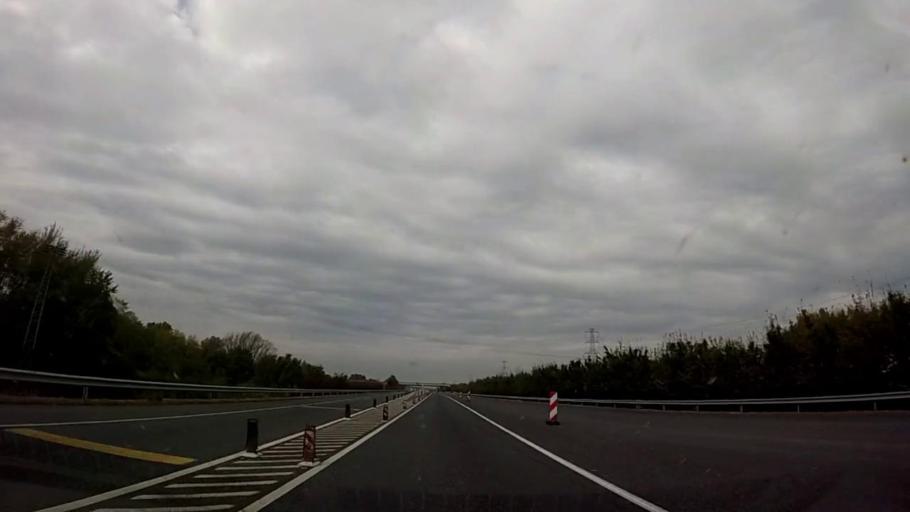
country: HR
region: Medimurska
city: Podturen
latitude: 46.5069
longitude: 16.5820
